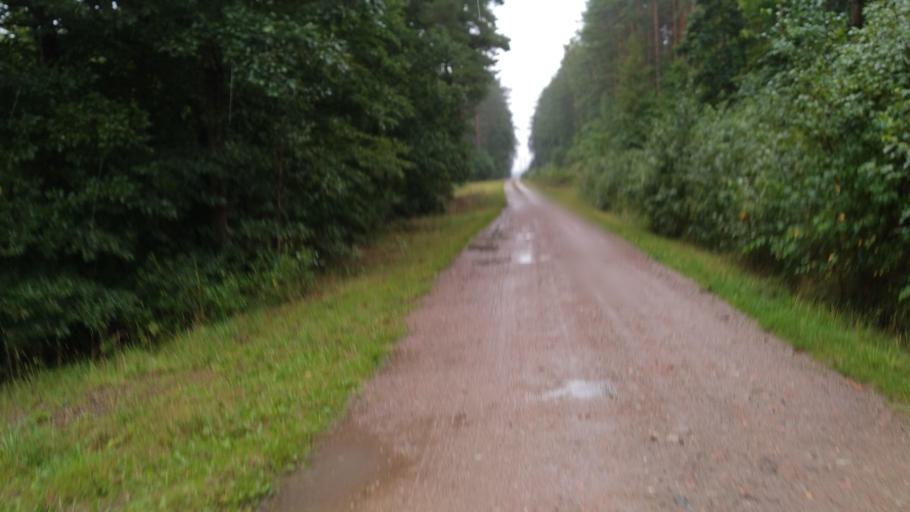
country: PL
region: Pomeranian Voivodeship
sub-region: Powiat wejherowski
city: Goscicino
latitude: 54.6207
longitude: 18.1521
